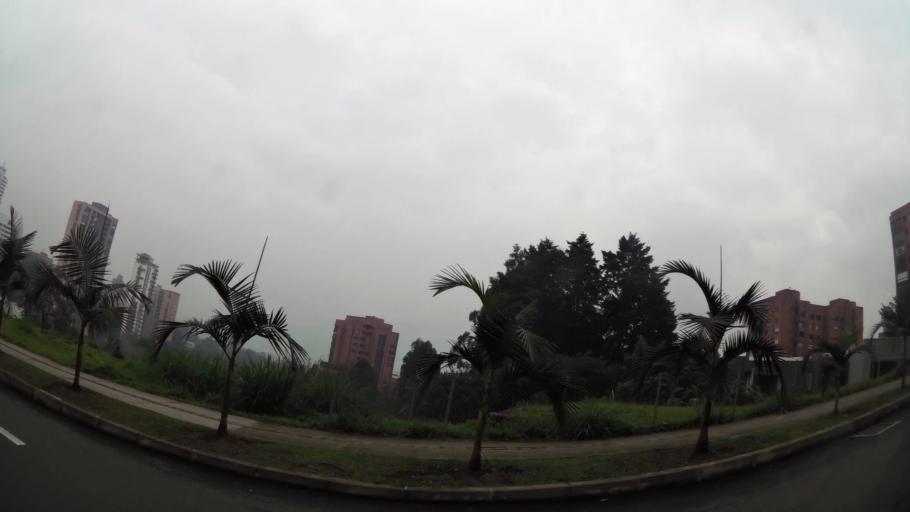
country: CO
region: Antioquia
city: Envigado
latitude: 6.1883
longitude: -75.5661
